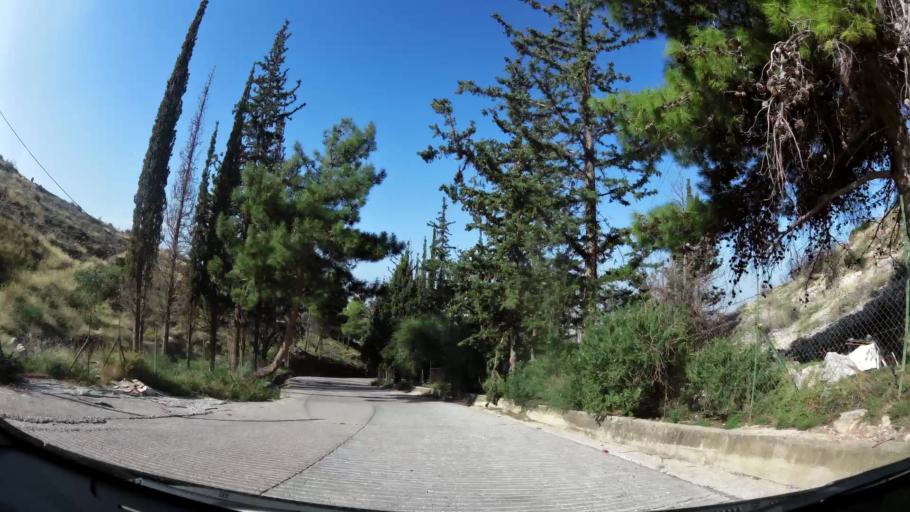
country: GR
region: Attica
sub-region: Nomarchia Athinas
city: Ilioupoli
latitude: 37.9431
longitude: 23.7764
